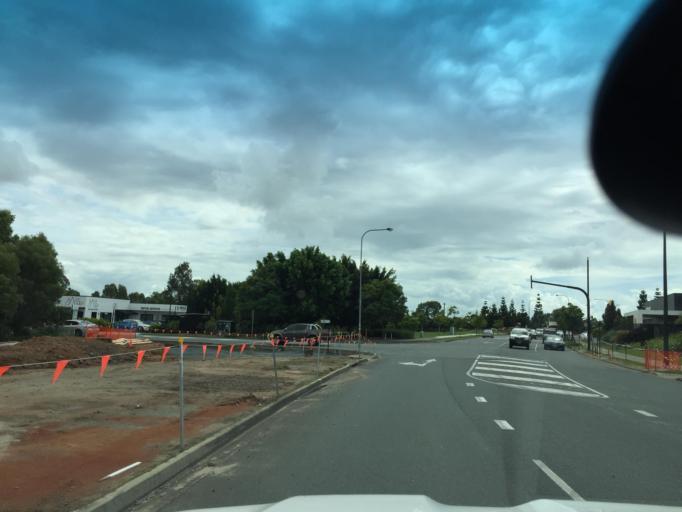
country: AU
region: Queensland
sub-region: Moreton Bay
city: Deception Bay
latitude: -27.2152
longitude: 152.9977
